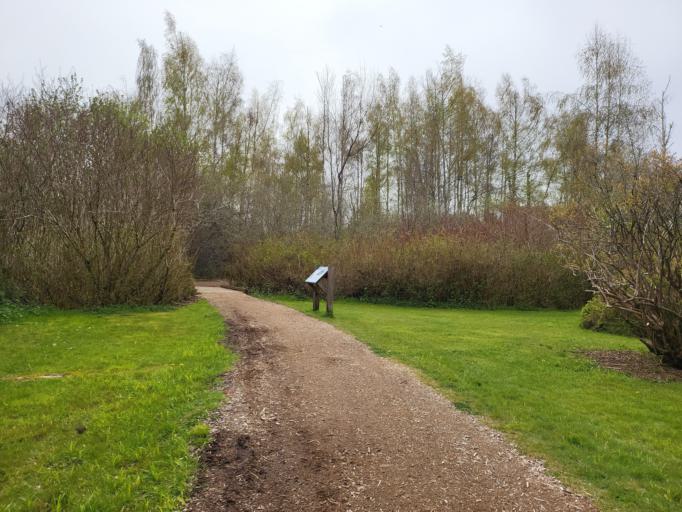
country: US
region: Washington
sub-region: King County
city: Newport
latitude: 47.5911
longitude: -122.1865
